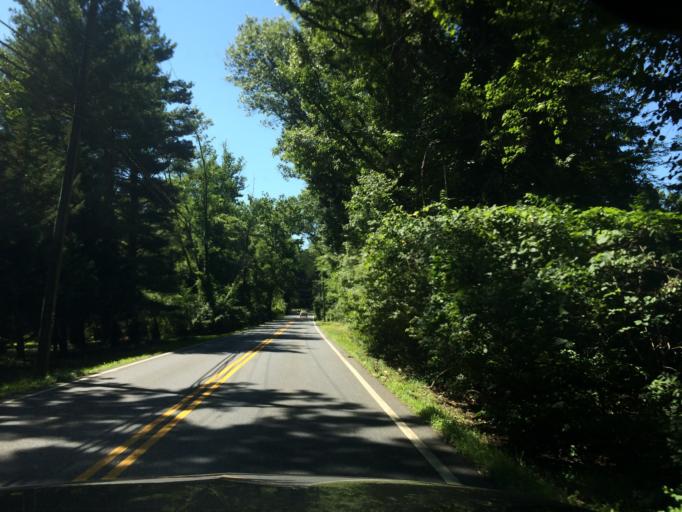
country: US
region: Maryland
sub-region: Baltimore County
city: Mays Chapel
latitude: 39.4241
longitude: -76.6865
